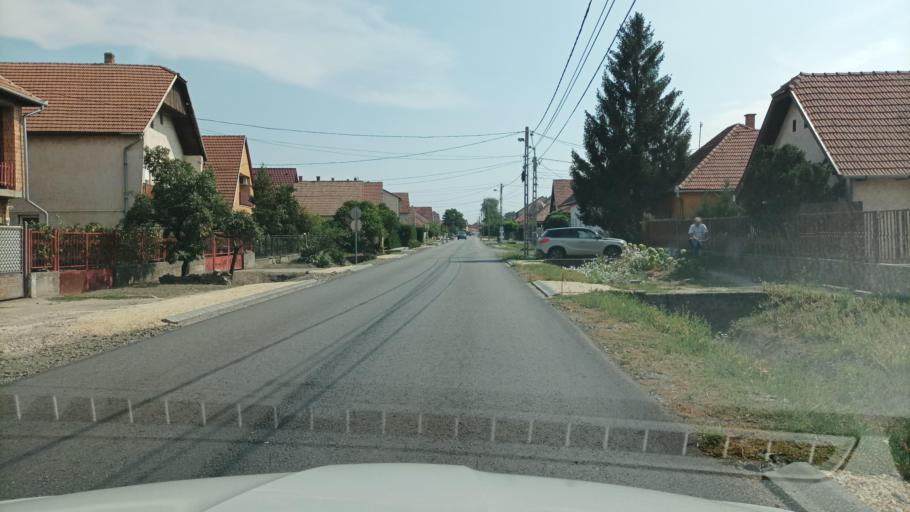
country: HU
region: Pest
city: Galgaheviz
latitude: 47.6139
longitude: 19.5829
